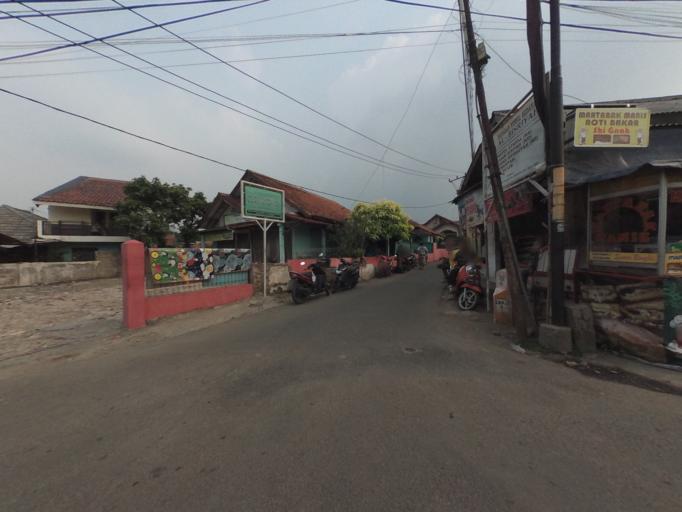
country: ID
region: West Java
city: Ciampea
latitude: -6.5660
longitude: 106.6738
